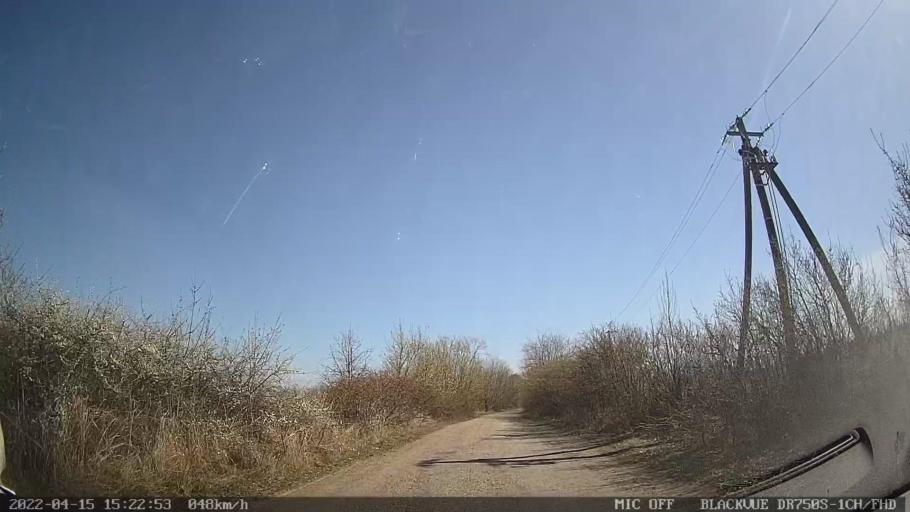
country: MD
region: Raionul Ocnita
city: Otaci
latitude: 48.3784
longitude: 27.9167
